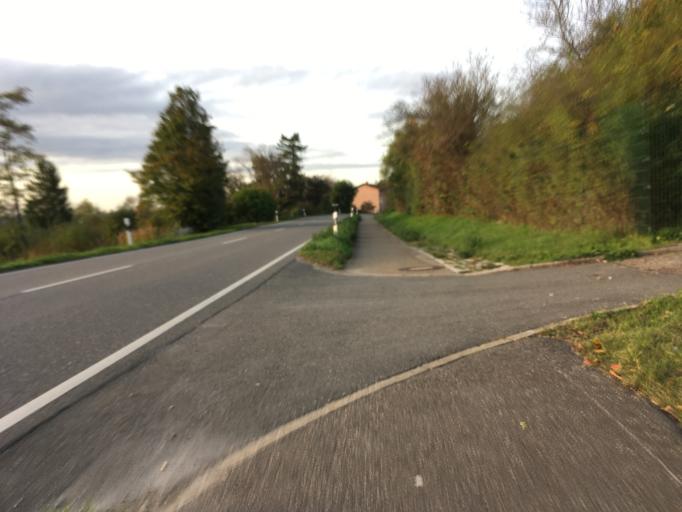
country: DE
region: Baden-Wuerttemberg
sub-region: Karlsruhe Region
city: Nussloch
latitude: 49.3136
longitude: 8.6987
